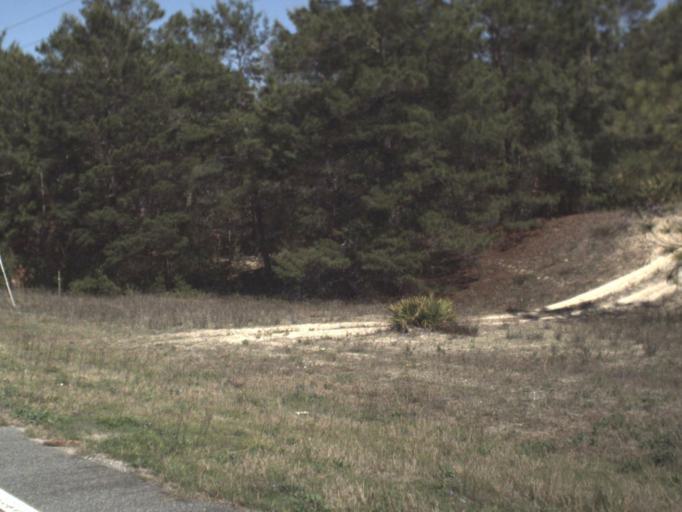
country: US
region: Florida
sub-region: Wakulla County
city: Crawfordville
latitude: 29.9332
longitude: -84.3949
